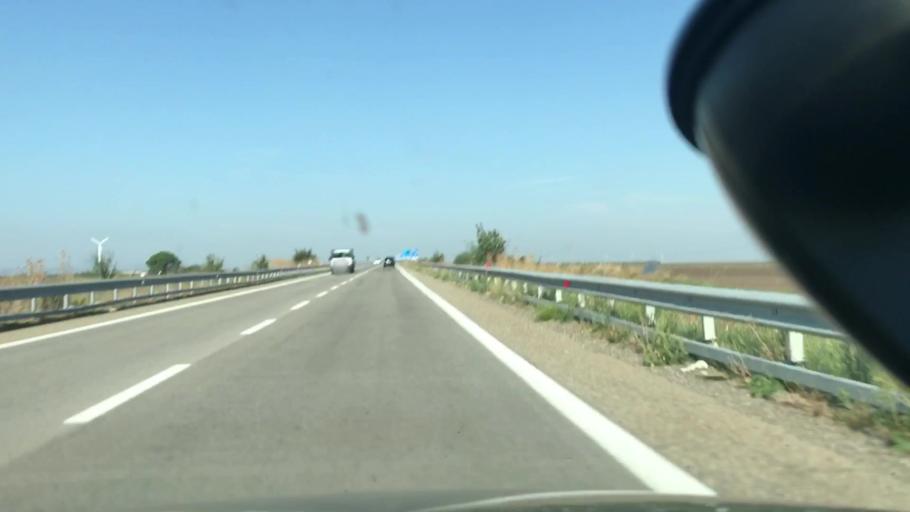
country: IT
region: Basilicate
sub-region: Provincia di Potenza
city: Montemilone
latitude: 40.9905
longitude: 15.8993
